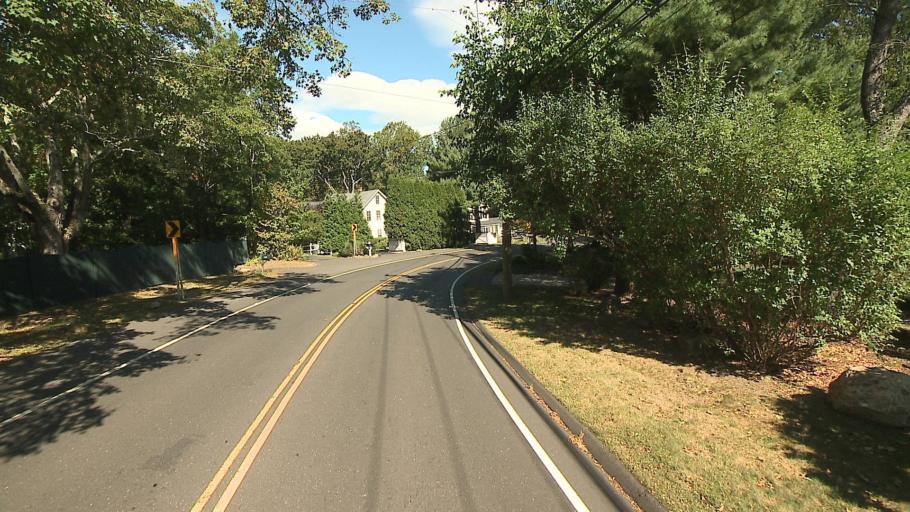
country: US
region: Connecticut
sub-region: Fairfield County
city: New Canaan
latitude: 41.1346
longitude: -73.4967
